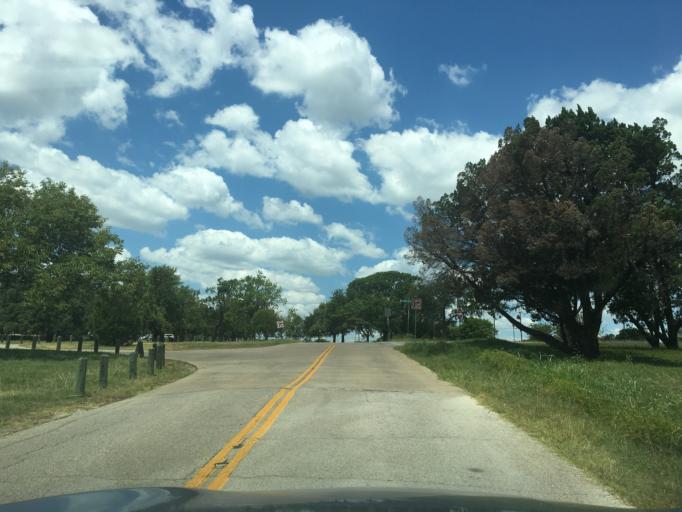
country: US
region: Texas
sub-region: Dallas County
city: Highland Park
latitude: 32.8621
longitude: -96.7225
